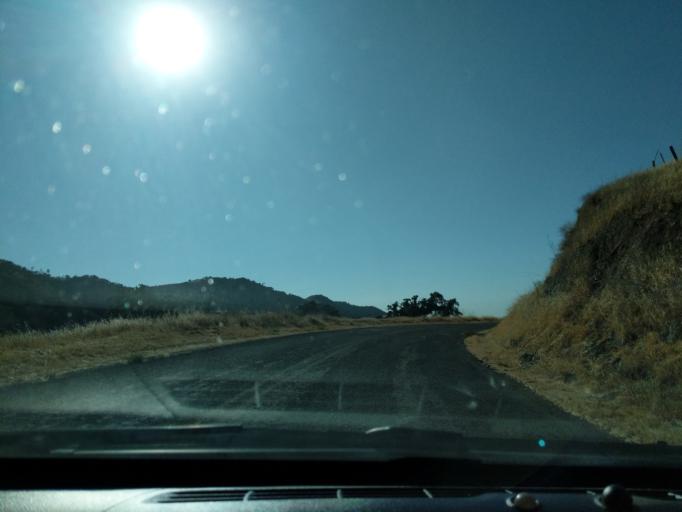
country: US
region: California
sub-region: Monterey County
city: King City
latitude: 36.1678
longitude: -120.7845
